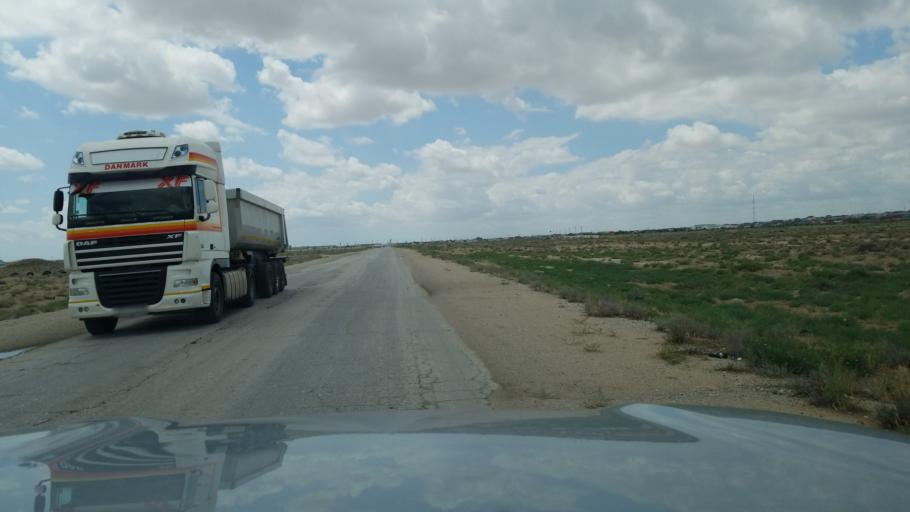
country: TM
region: Balkan
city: Balkanabat
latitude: 39.4882
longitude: 54.4088
